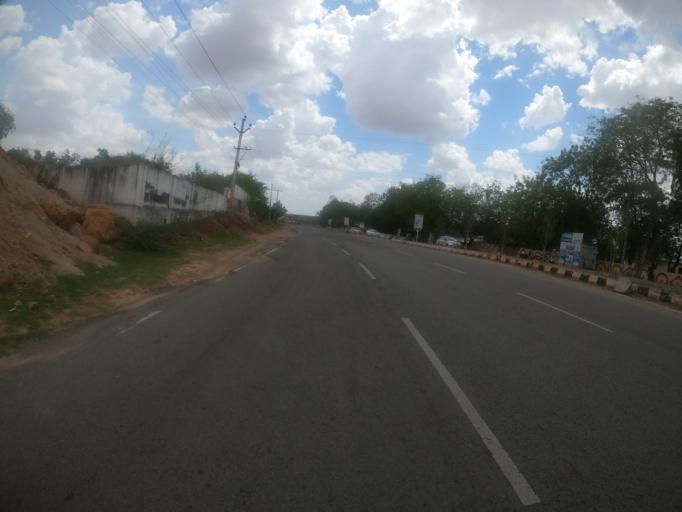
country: IN
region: Telangana
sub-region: Rangareddi
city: Sriramnagar
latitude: 17.3311
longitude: 78.2884
